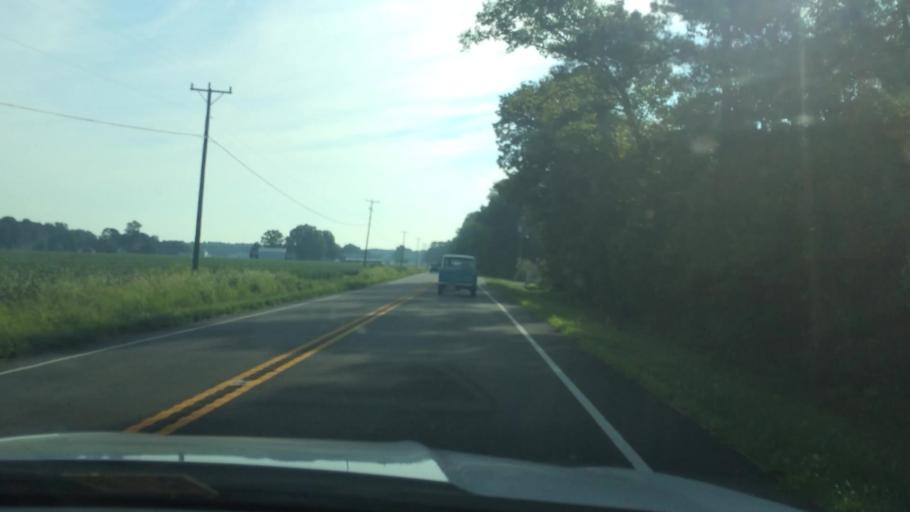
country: US
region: Virginia
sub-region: Middlesex County
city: Deltaville
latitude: 37.4914
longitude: -76.4243
